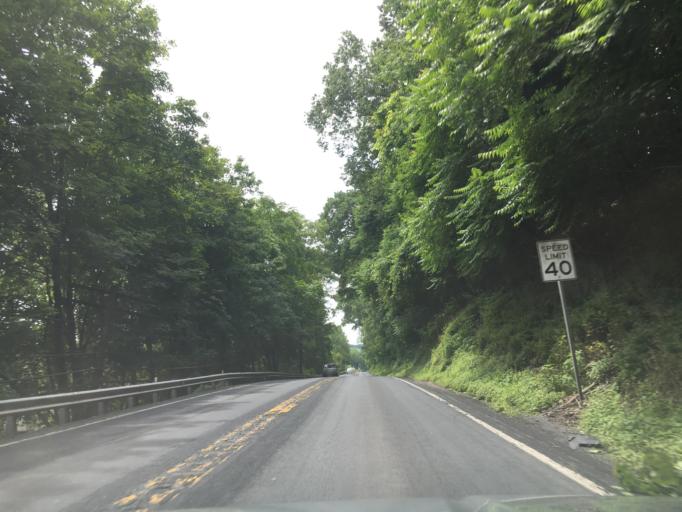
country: US
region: Pennsylvania
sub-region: Lehigh County
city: Laurys Station
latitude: 40.7175
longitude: -75.5258
